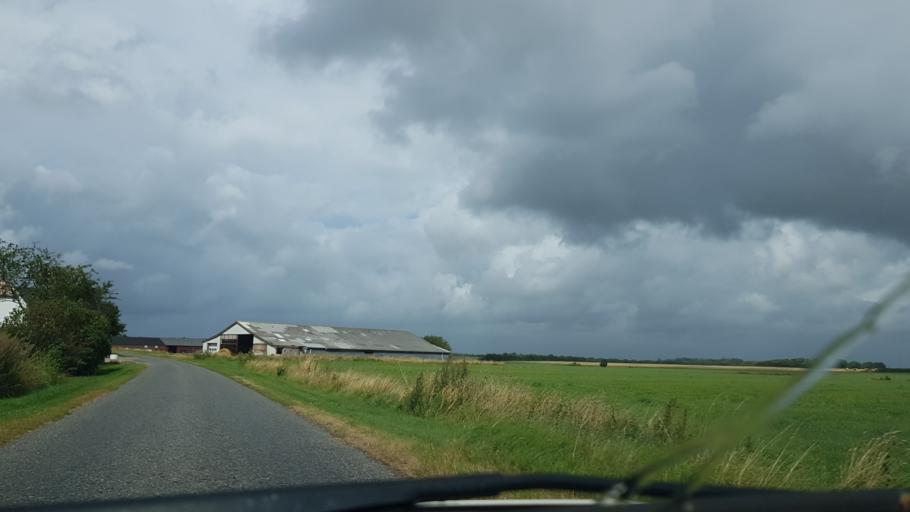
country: DK
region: South Denmark
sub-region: Esbjerg Kommune
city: Ribe
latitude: 55.2606
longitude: 8.8025
